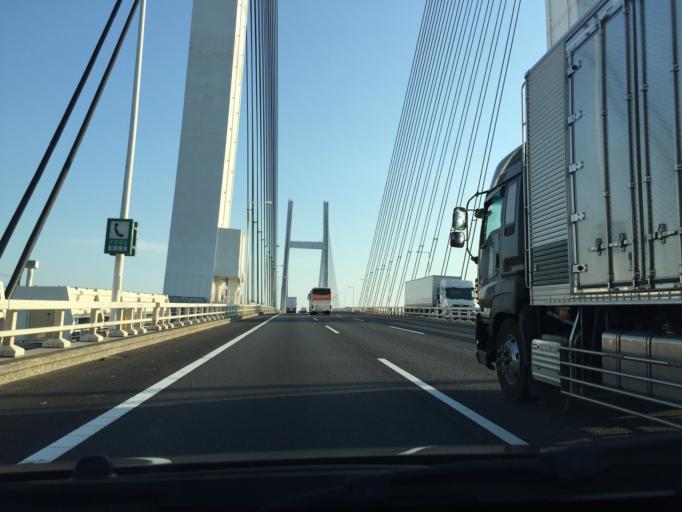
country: JP
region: Kanagawa
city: Yokohama
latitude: 35.4569
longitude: 139.6756
